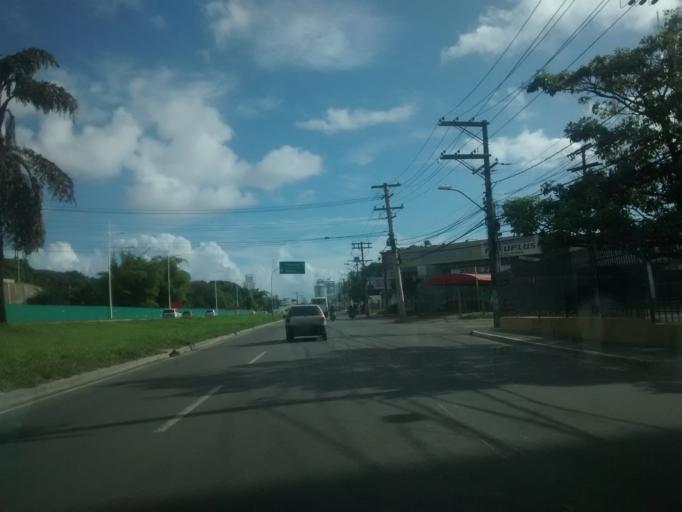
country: BR
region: Bahia
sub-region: Salvador
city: Salvador
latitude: -12.9686
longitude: -38.4414
